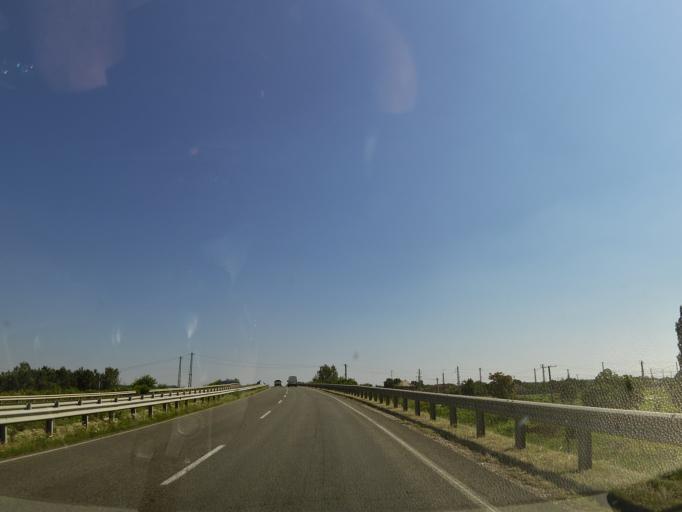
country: HU
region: Jasz-Nagykun-Szolnok
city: Szajol
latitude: 47.1703
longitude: 20.2820
